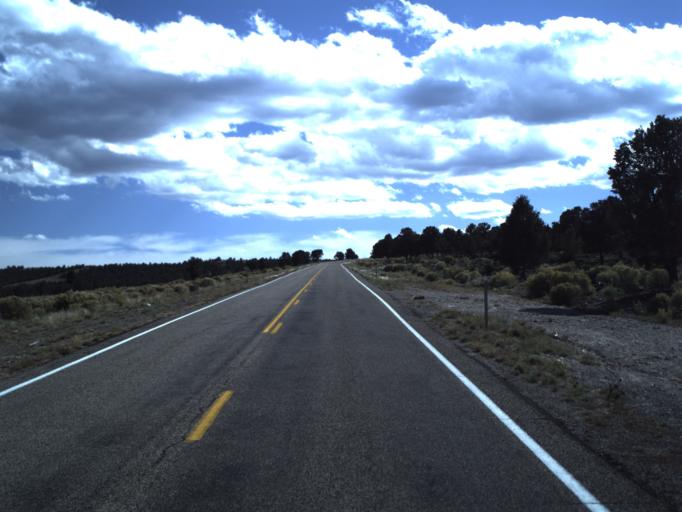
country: US
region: Utah
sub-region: Garfield County
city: Panguitch
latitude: 37.7948
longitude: -112.4371
